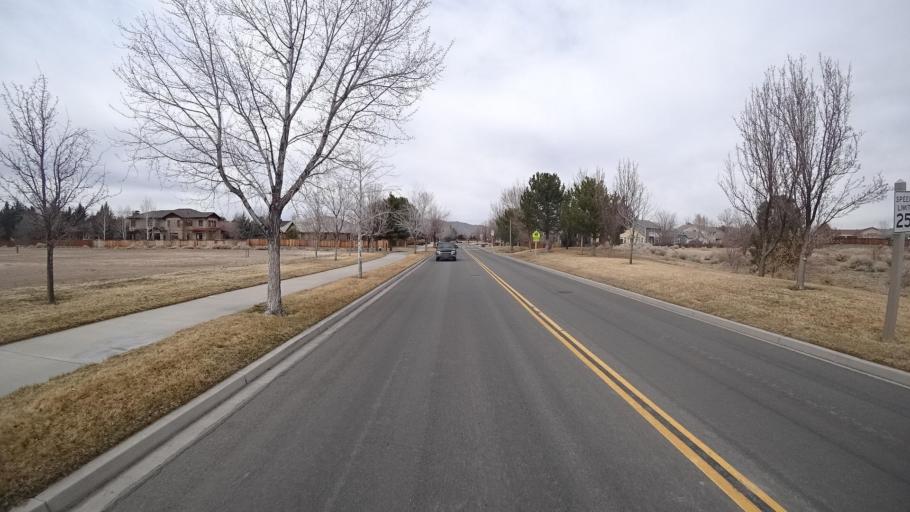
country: US
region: Nevada
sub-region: Washoe County
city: Spanish Springs
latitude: 39.6211
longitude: -119.6817
